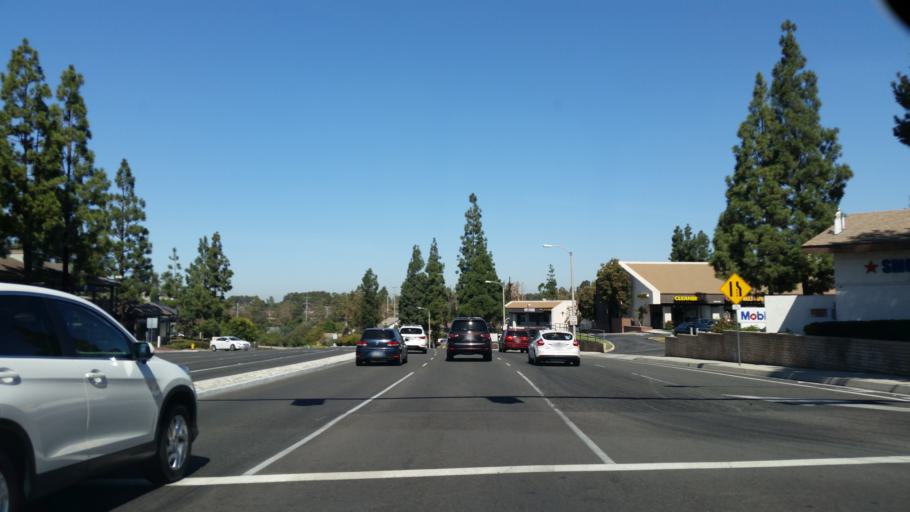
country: US
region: California
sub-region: Orange County
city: Lake Forest
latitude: 33.6469
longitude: -117.6859
